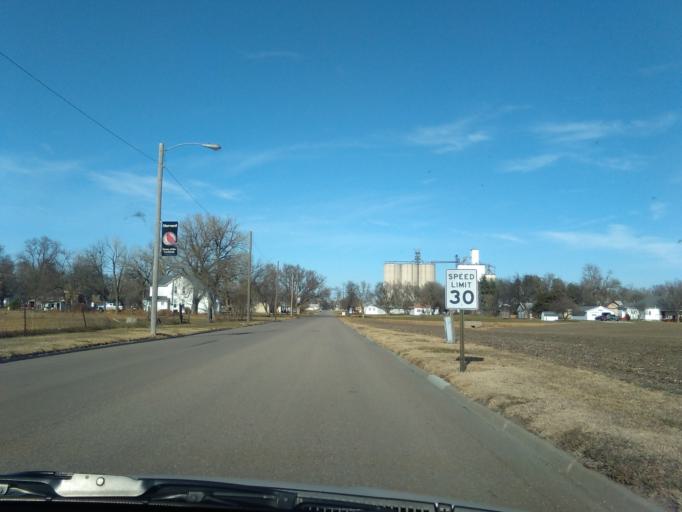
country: US
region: Nebraska
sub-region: Clay County
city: Harvard
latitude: 40.6119
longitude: -98.0971
